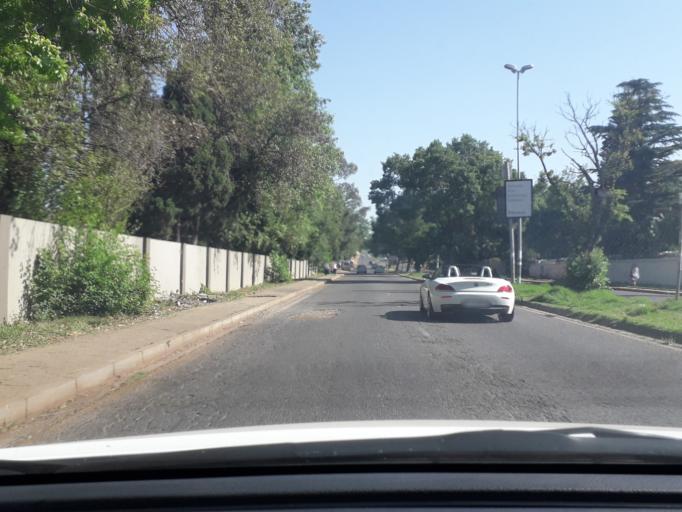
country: ZA
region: Gauteng
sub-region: City of Johannesburg Metropolitan Municipality
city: Johannesburg
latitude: -26.1235
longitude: 27.9739
